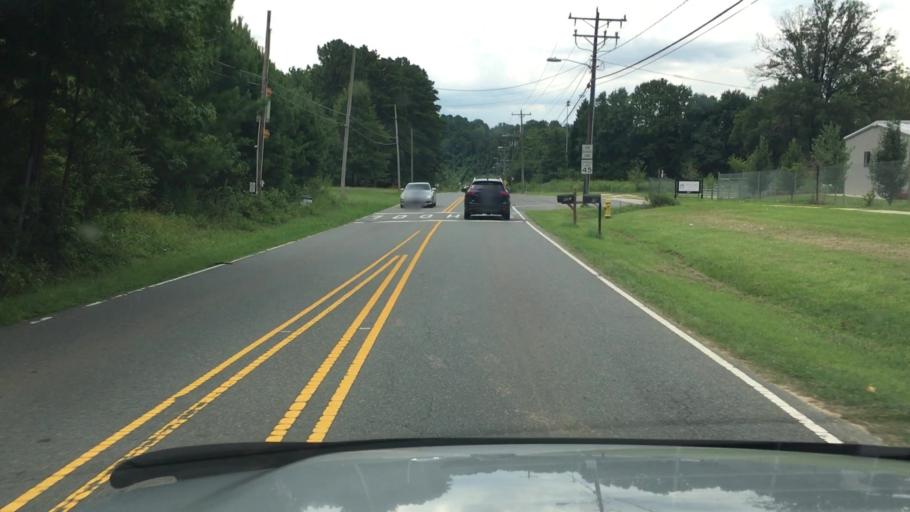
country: US
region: North Carolina
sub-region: Mecklenburg County
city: Huntersville
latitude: 35.3232
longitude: -80.8661
